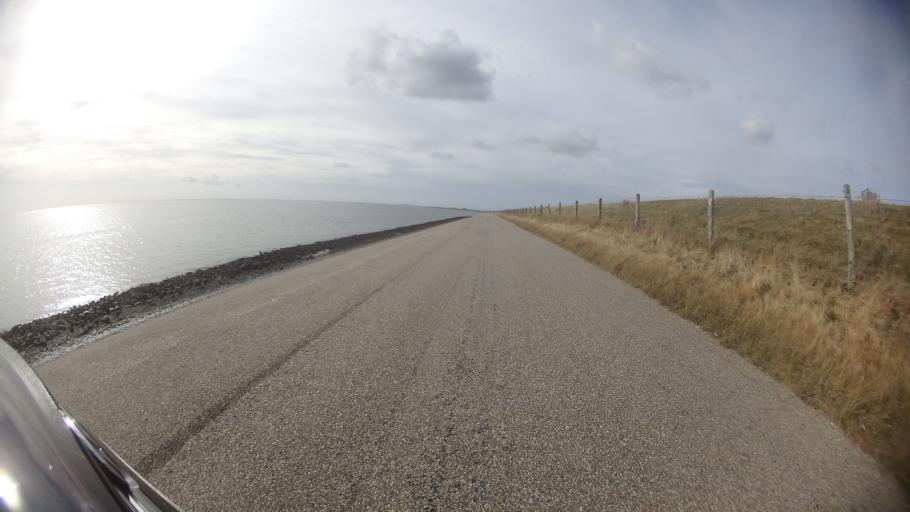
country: NL
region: North Holland
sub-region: Gemeente Texel
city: Den Burg
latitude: 53.0758
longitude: 4.8922
